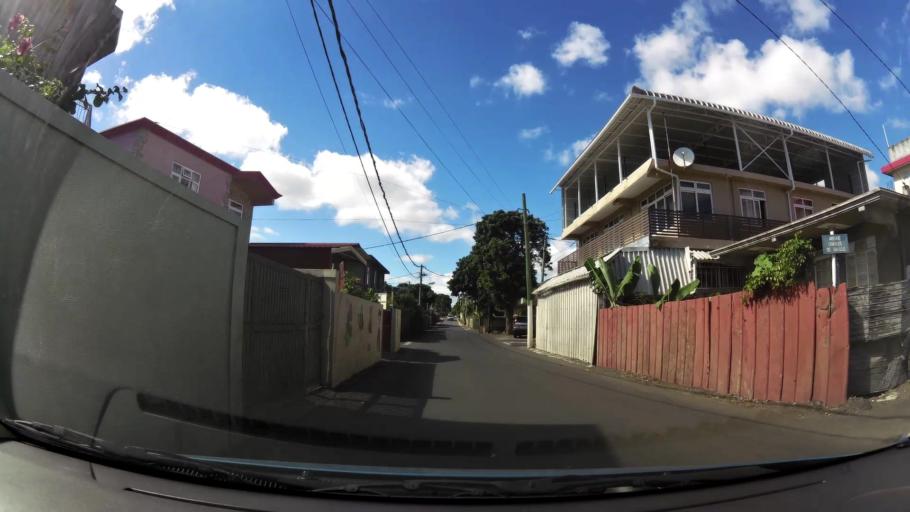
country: MU
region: Plaines Wilhems
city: Vacoas
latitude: -20.3015
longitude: 57.4799
